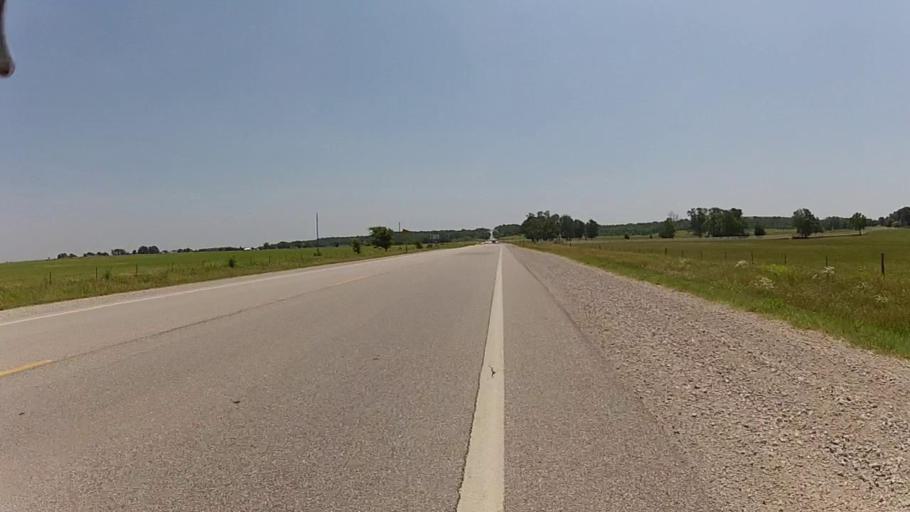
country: US
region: Kansas
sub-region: Montgomery County
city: Cherryvale
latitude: 37.2241
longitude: -95.5934
